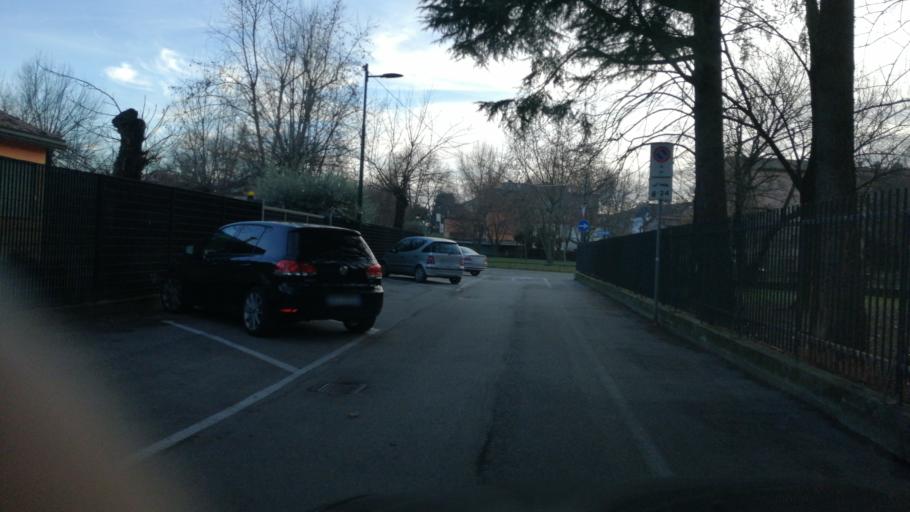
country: IT
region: Veneto
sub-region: Provincia di Venezia
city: Zelarino
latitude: 45.4867
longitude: 12.2130
